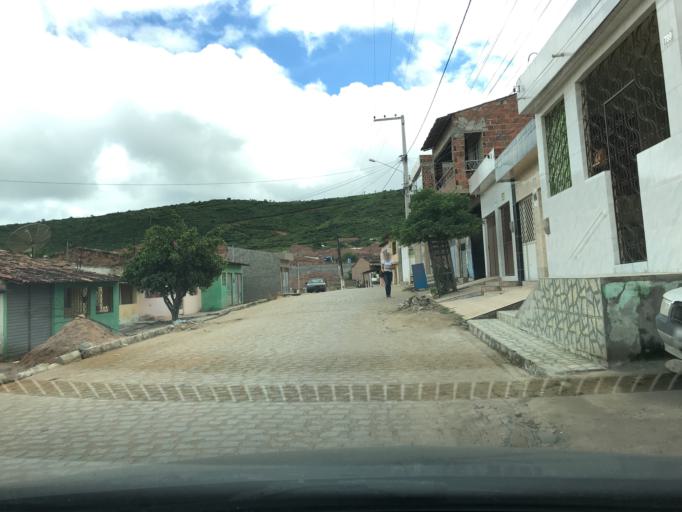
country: BR
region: Pernambuco
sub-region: Bezerros
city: Bezerros
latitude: -8.2284
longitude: -35.7607
